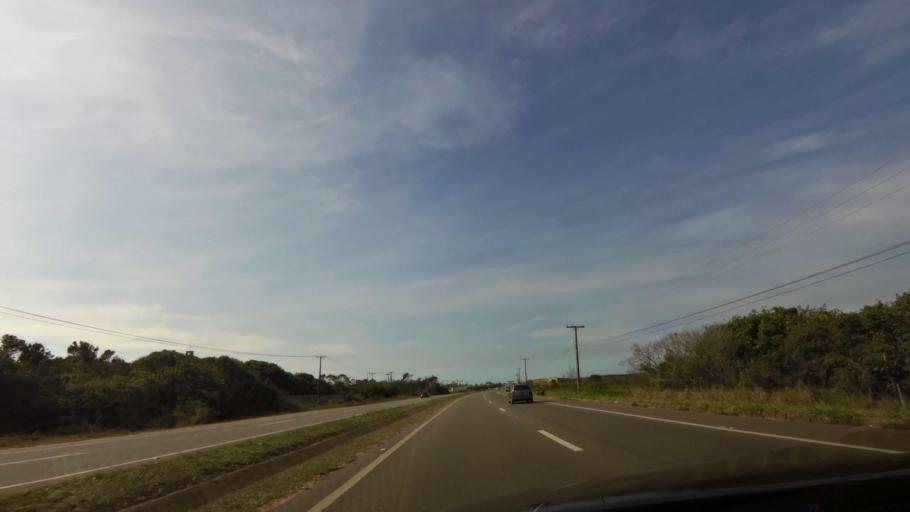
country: BR
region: Espirito Santo
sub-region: Vila Velha
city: Vila Velha
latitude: -20.4594
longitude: -40.3429
